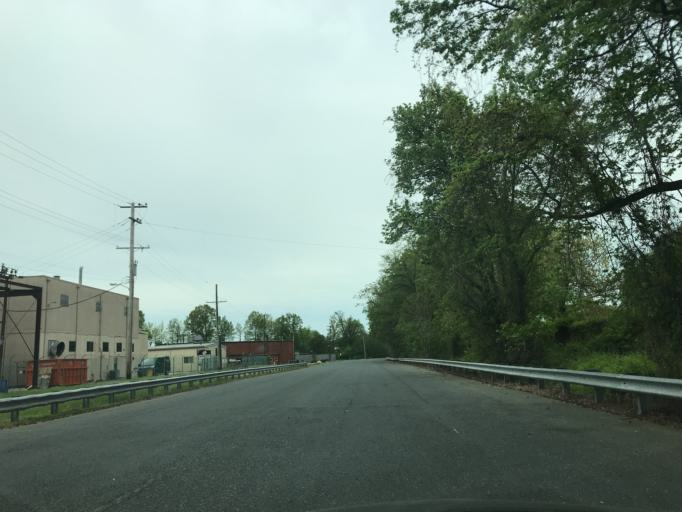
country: US
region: Maryland
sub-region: Baltimore County
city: Edgemere
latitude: 39.2569
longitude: -76.4651
